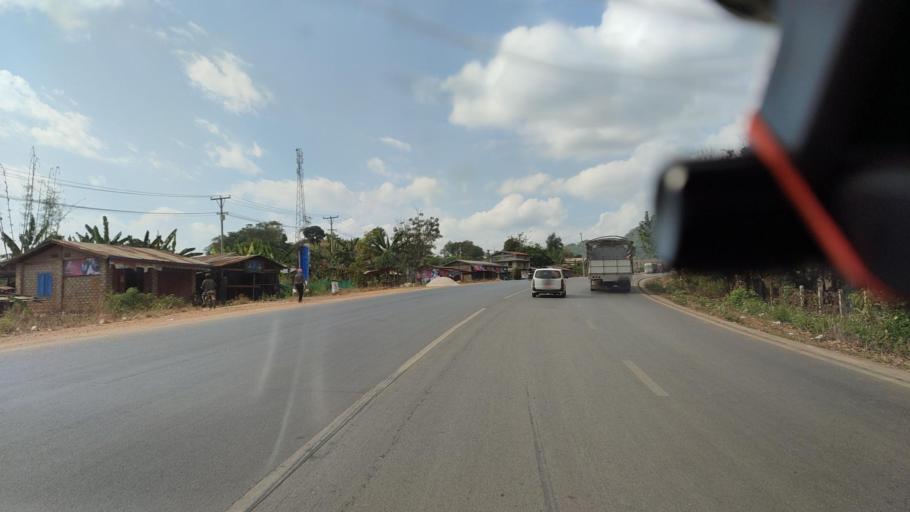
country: MM
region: Shan
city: Lashio
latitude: 23.0856
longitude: 97.7978
